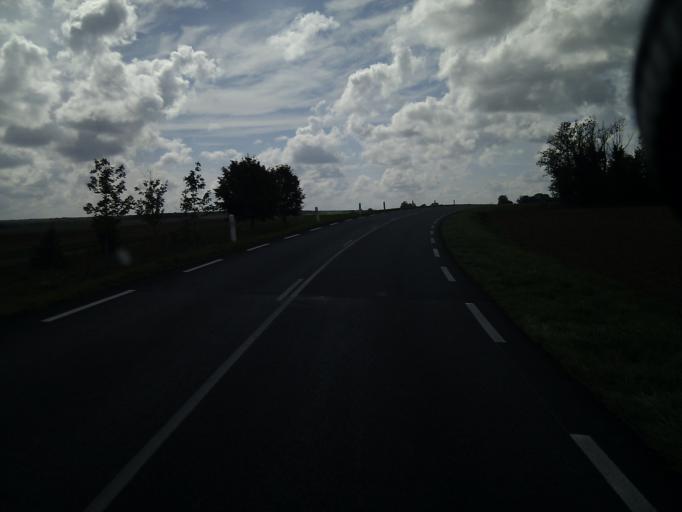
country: FR
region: Bourgogne
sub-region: Departement de la Cote-d'Or
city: Montbard
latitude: 47.7142
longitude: 4.4462
